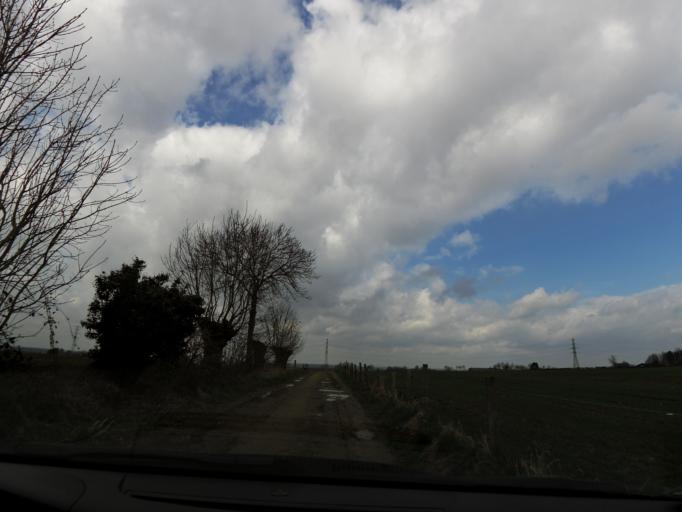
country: NL
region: Limburg
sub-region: Gemeente Voerendaal
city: Ubachsberg
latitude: 50.8545
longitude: 5.9389
